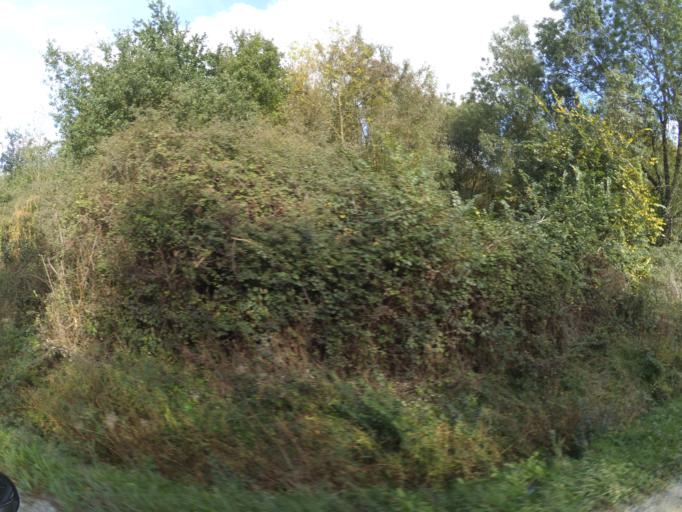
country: FR
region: Pays de la Loire
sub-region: Departement de la Loire-Atlantique
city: Le Loroux-Bottereau
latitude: 47.2253
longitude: -1.3705
